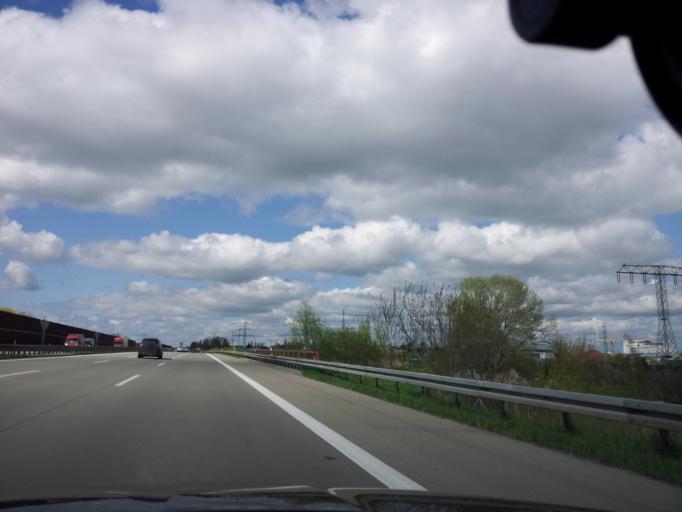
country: DE
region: Brandenburg
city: Neuenhagen
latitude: 52.5275
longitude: 13.7127
